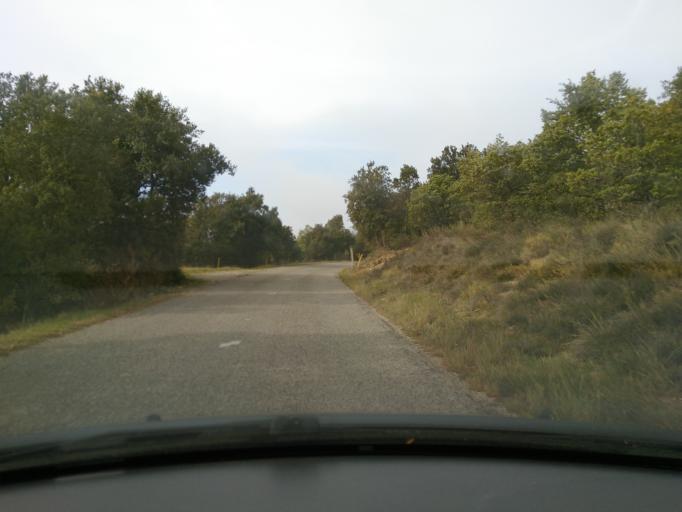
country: FR
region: Rhone-Alpes
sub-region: Departement de l'Ardeche
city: Ruoms
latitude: 44.4519
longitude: 4.3926
